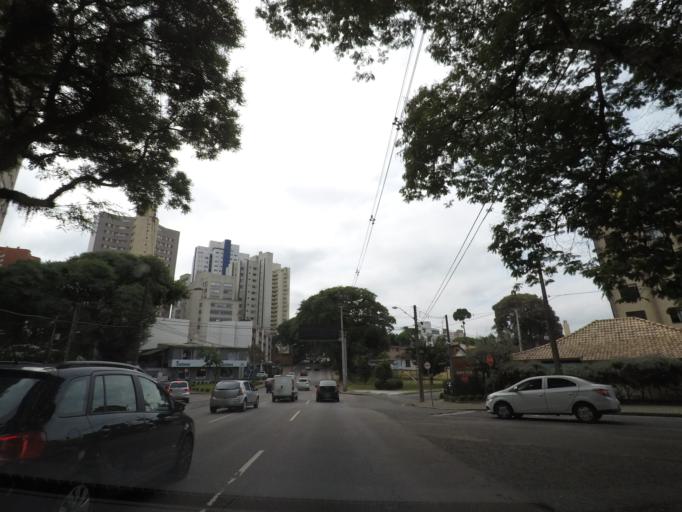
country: BR
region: Parana
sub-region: Curitiba
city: Curitiba
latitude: -25.4555
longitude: -49.2855
